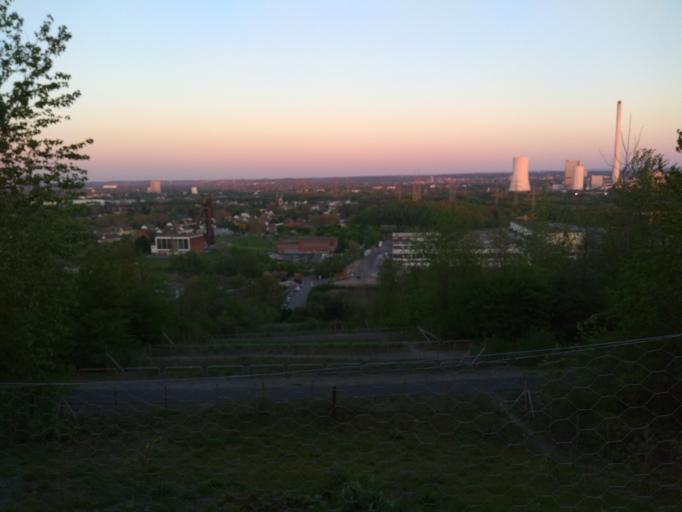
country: DE
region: North Rhine-Westphalia
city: Herten
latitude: 51.5660
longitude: 7.1713
